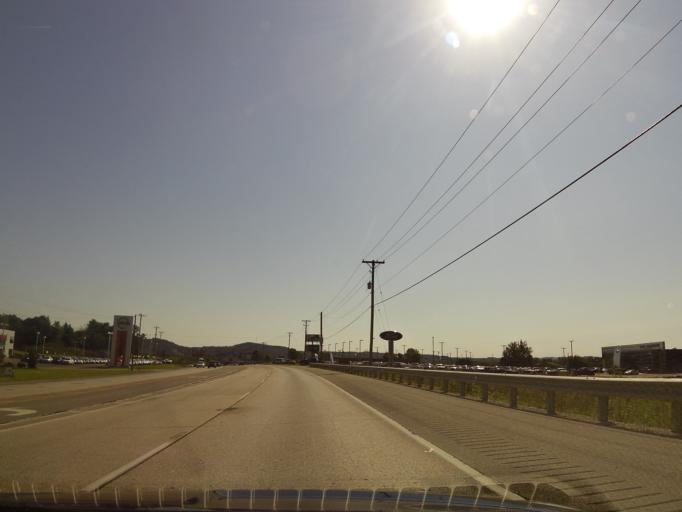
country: US
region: Kentucky
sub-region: Laurel County
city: London
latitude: 37.1050
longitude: -84.0804
